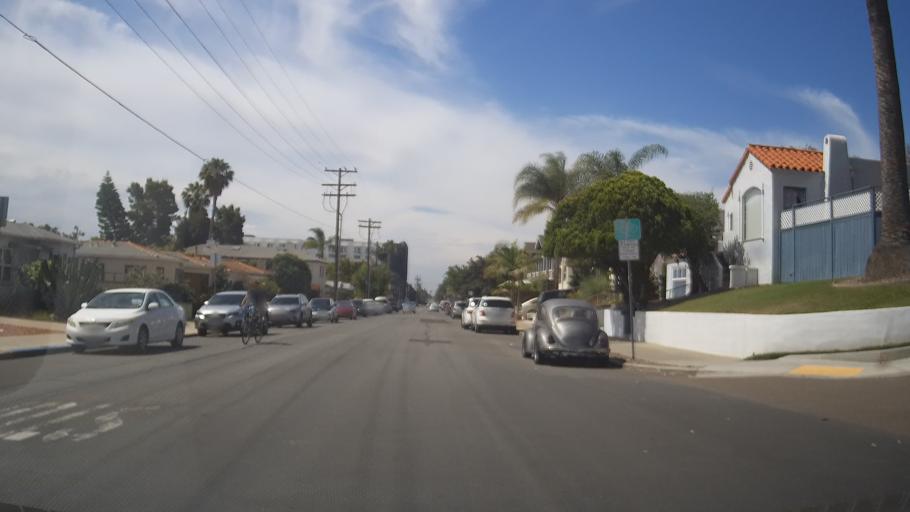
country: US
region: California
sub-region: San Diego County
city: San Diego
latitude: 32.7586
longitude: -117.1438
